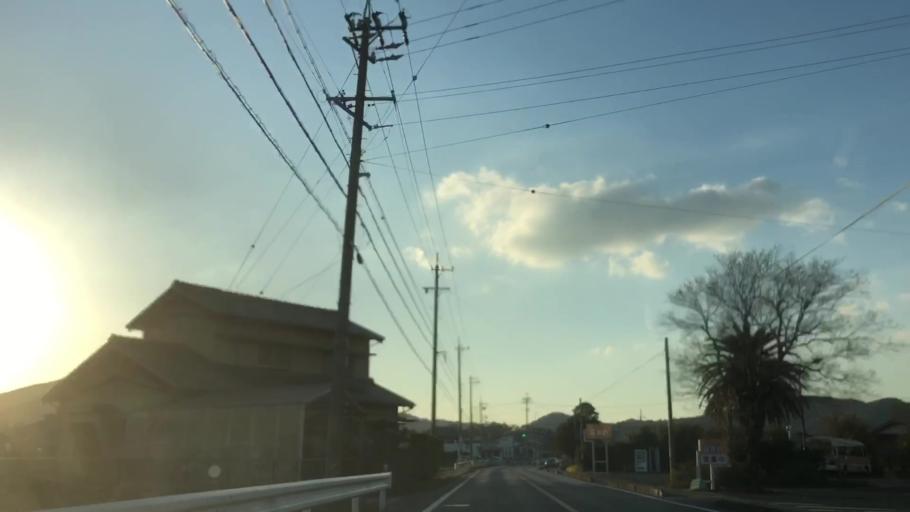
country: JP
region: Aichi
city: Tahara
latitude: 34.6540
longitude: 137.2098
